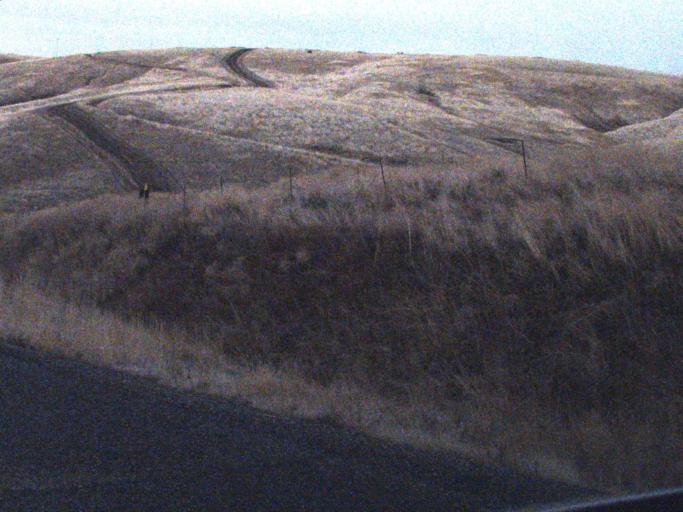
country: US
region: Washington
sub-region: Garfield County
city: Pomeroy
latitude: 46.5556
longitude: -117.7697
